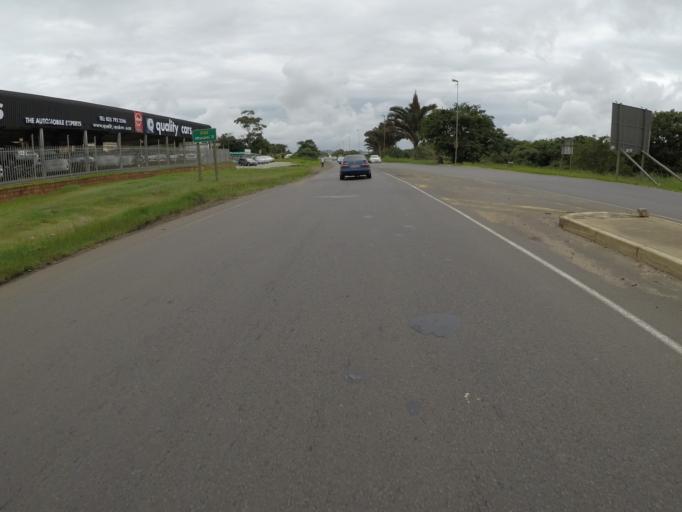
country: ZA
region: KwaZulu-Natal
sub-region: uThungulu District Municipality
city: Empangeni
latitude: -28.7646
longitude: 31.9067
